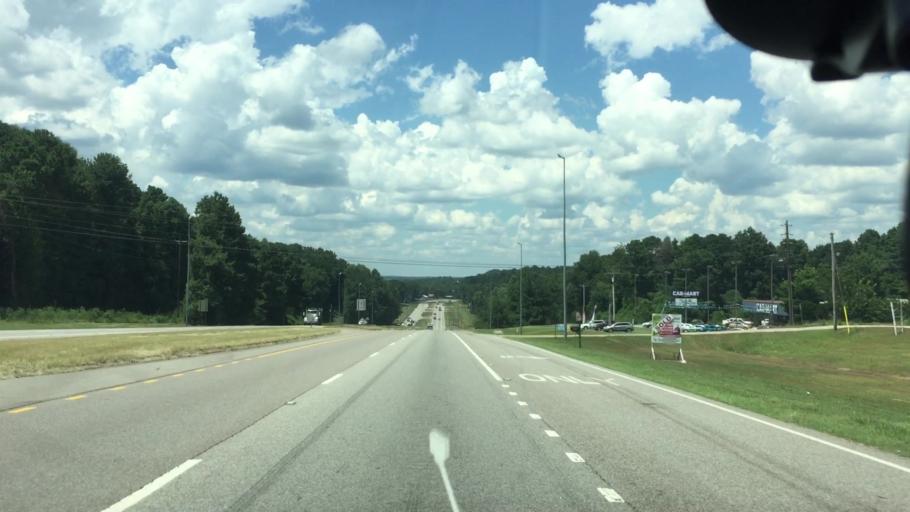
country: US
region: Alabama
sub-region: Pike County
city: Troy
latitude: 31.8124
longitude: -85.9911
